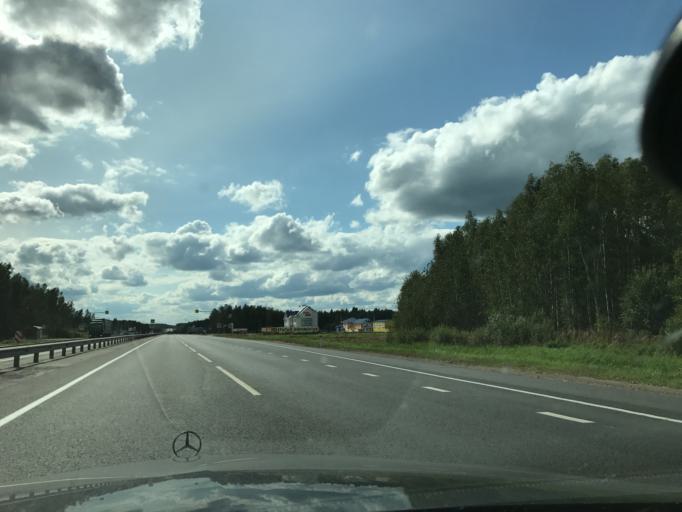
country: RU
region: Vladimir
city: Sudogda
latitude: 56.1367
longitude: 40.8906
